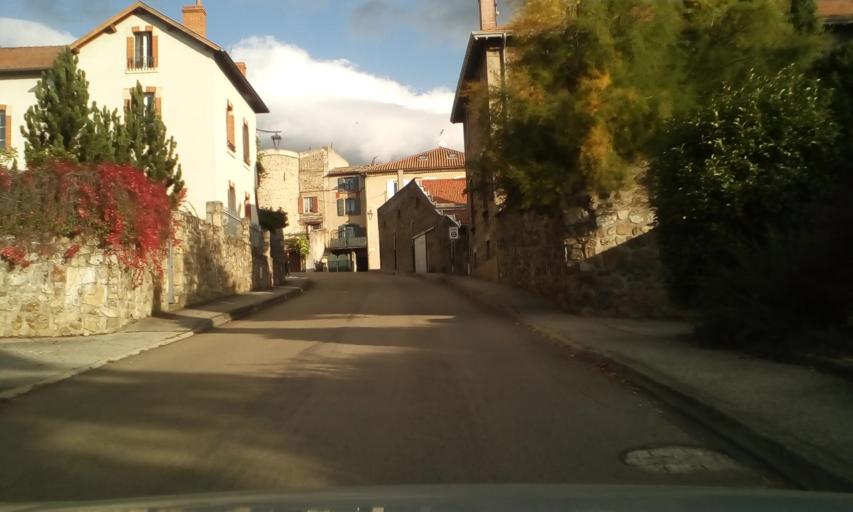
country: FR
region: Rhone-Alpes
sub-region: Departement de l'Ardeche
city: Boulieu-les-Annonay
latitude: 45.2680
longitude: 4.6721
